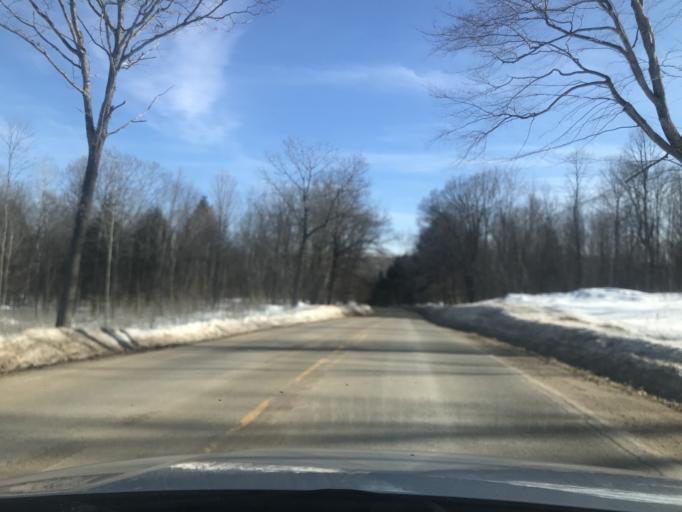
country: US
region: Michigan
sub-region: Dickinson County
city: Kingsford
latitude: 45.4039
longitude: -88.3770
